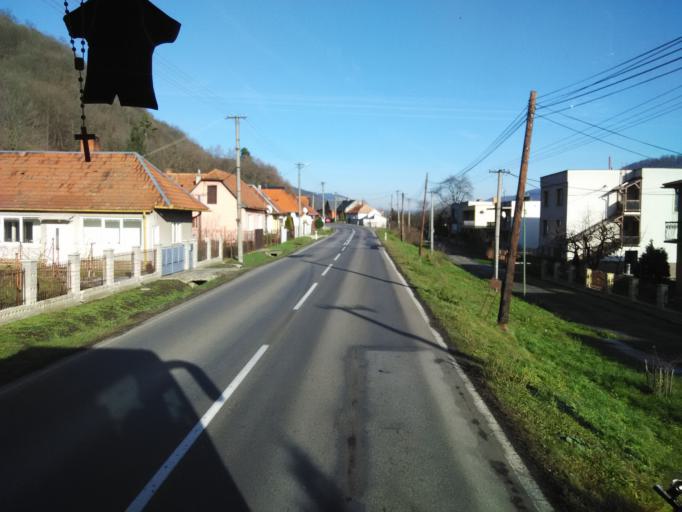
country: SK
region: Nitriansky
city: Tlmace
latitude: 48.3525
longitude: 18.5681
